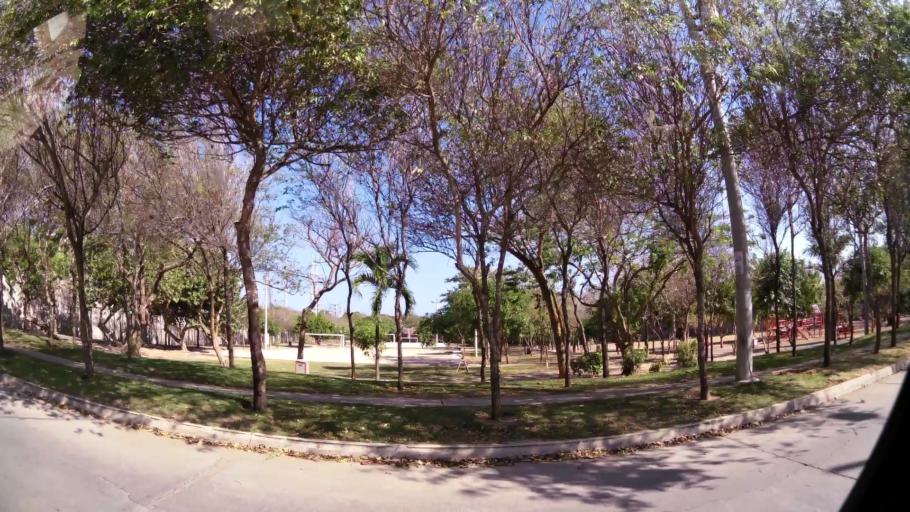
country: CO
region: Atlantico
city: Barranquilla
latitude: 11.0243
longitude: -74.8105
